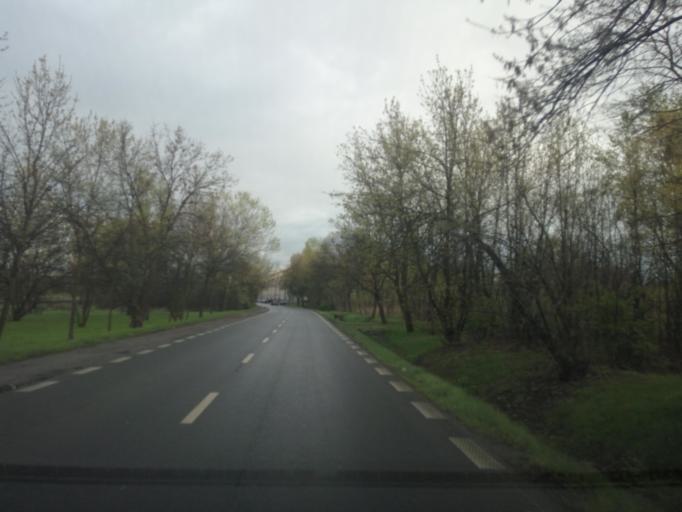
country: PL
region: Lower Silesian Voivodeship
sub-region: Powiat wroclawski
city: Radwanice
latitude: 51.0715
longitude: 17.0786
